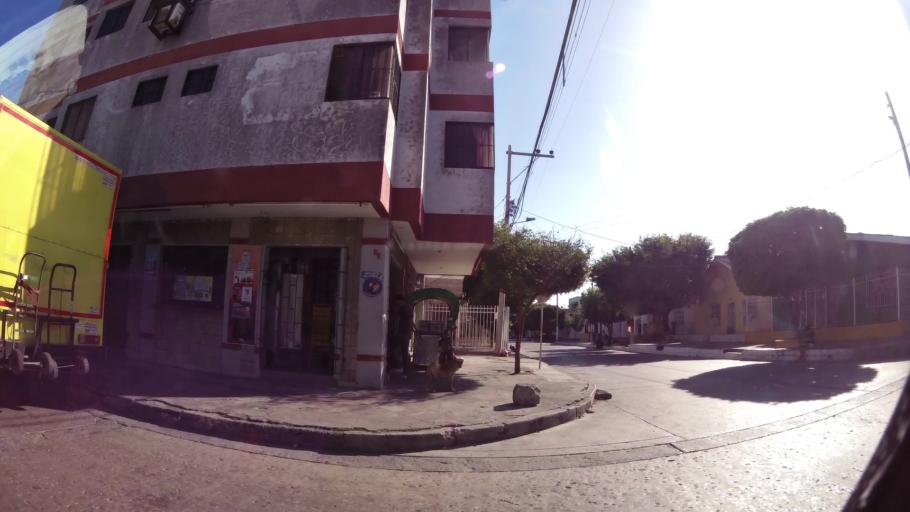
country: CO
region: Atlantico
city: Barranquilla
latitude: 10.9726
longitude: -74.7912
